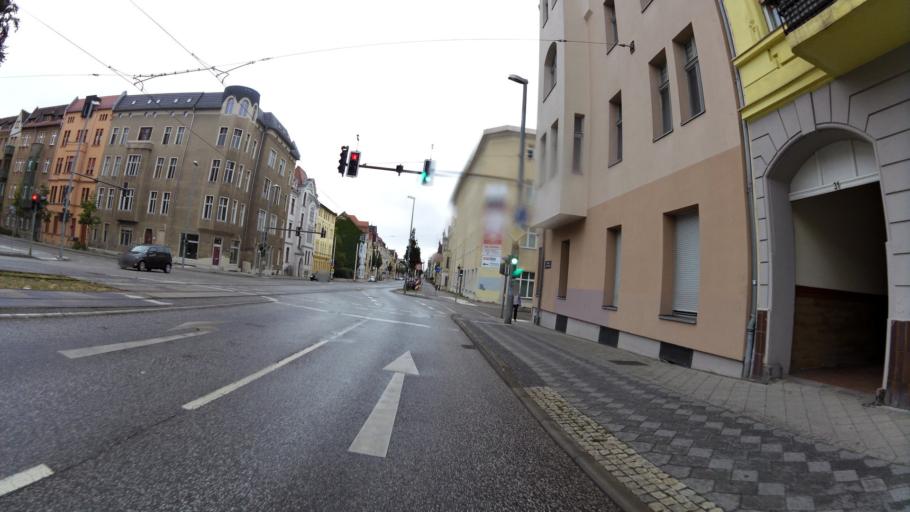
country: DE
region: Brandenburg
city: Cottbus
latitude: 51.7539
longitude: 14.3285
